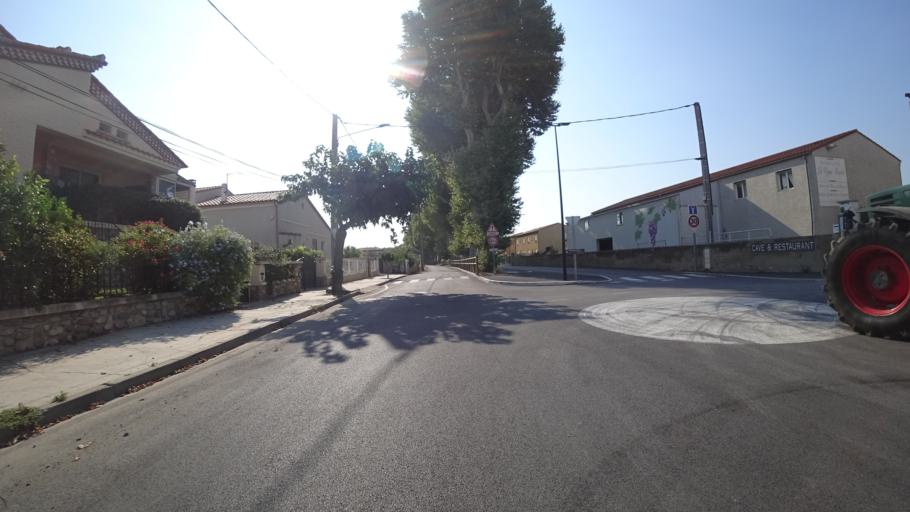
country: FR
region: Languedoc-Roussillon
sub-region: Departement des Pyrenees-Orientales
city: Claira
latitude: 42.7605
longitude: 2.9589
